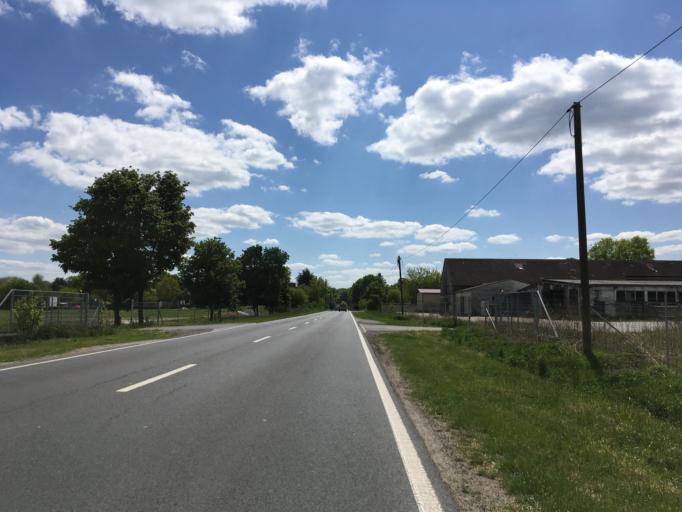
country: DE
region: Brandenburg
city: Rudnitz
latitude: 52.7651
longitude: 13.5654
